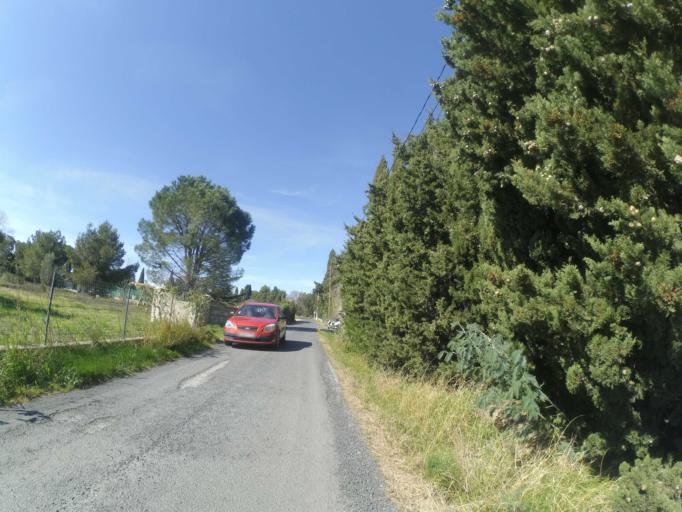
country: FR
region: Languedoc-Roussillon
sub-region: Departement des Pyrenees-Orientales
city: Le Soler
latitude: 42.6772
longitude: 2.7981
